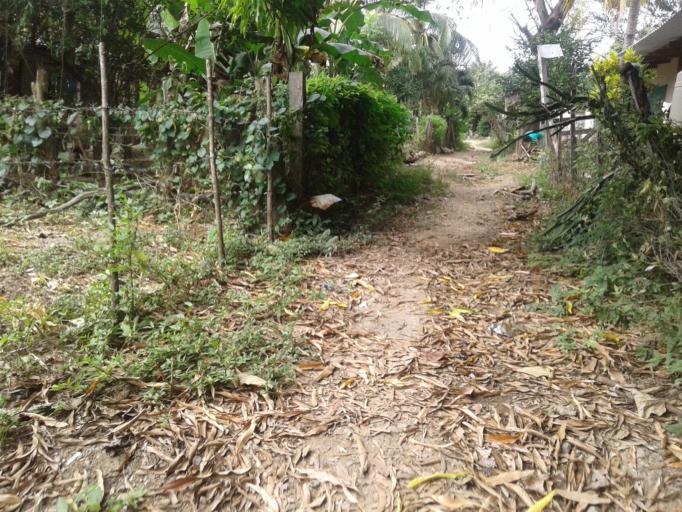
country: CR
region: Guanacaste
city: La Cruz
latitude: 11.1108
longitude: -85.7603
